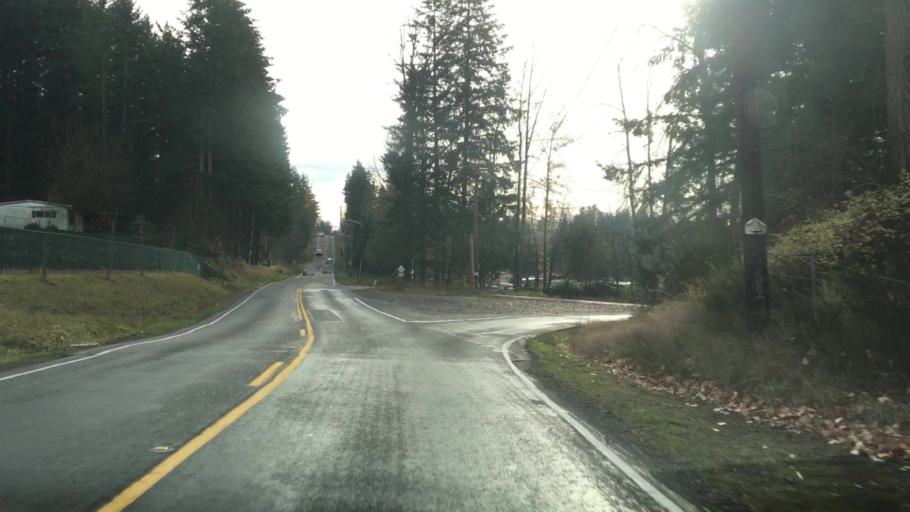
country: US
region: Washington
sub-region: Pierce County
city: Frederickson
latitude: 47.1156
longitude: -122.3255
